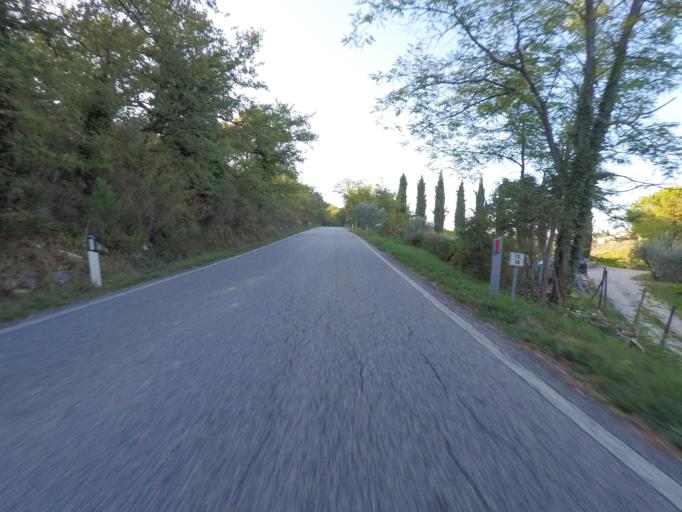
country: IT
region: Tuscany
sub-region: Provincia di Siena
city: Radda in Chianti
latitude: 43.4789
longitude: 11.3695
